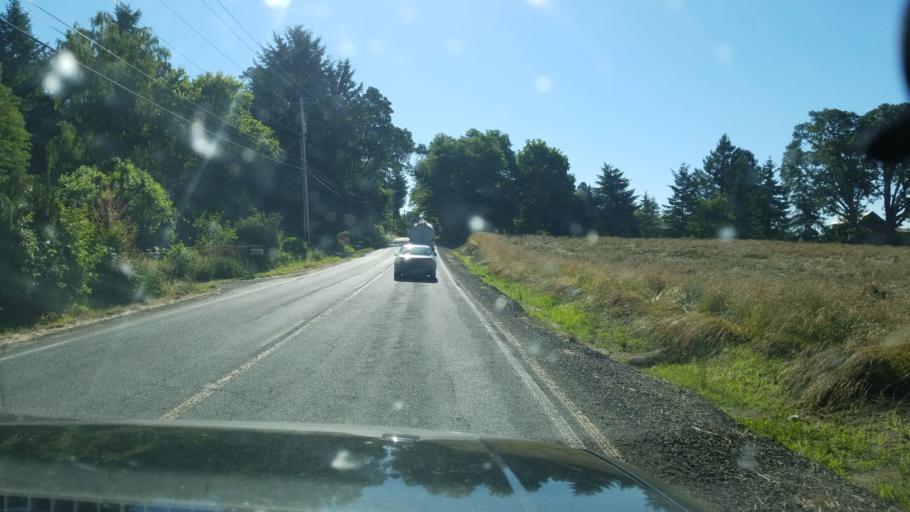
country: US
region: Oregon
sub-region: Yamhill County
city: Carlton
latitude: 45.2943
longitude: -123.1983
